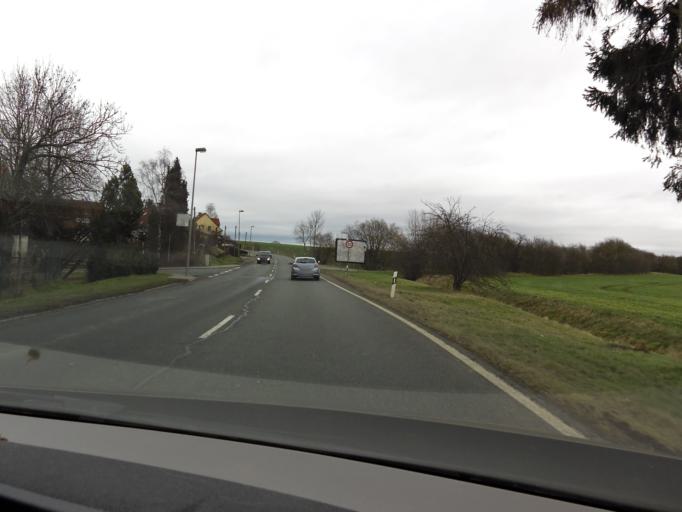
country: DE
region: Thuringia
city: Umpferstedt
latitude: 50.9760
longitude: 11.4164
